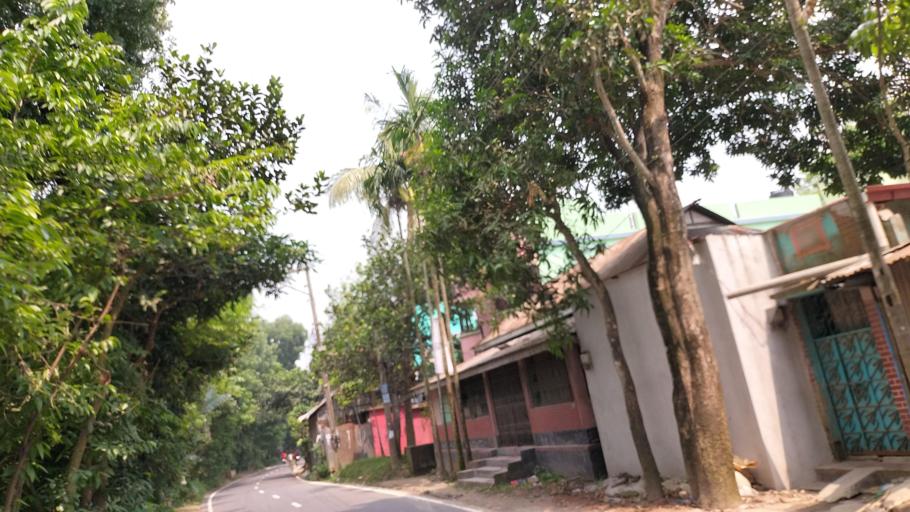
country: BD
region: Dhaka
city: Azimpur
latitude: 23.7143
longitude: 90.2802
